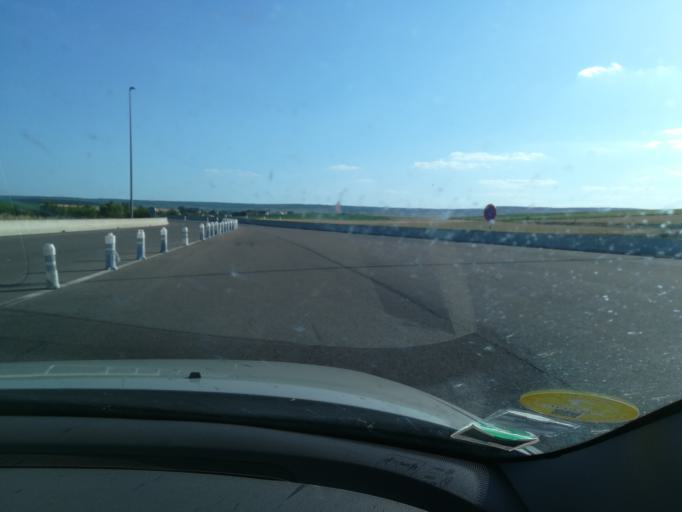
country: FR
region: Champagne-Ardenne
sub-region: Departement de la Marne
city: Bezannes
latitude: 49.2050
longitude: 4.0059
